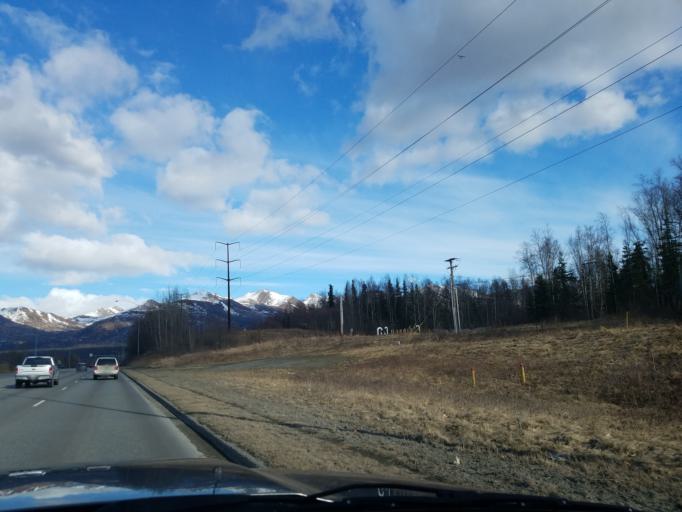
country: US
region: Alaska
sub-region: Anchorage Municipality
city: Elmendorf Air Force Base
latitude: 61.1807
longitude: -149.7563
